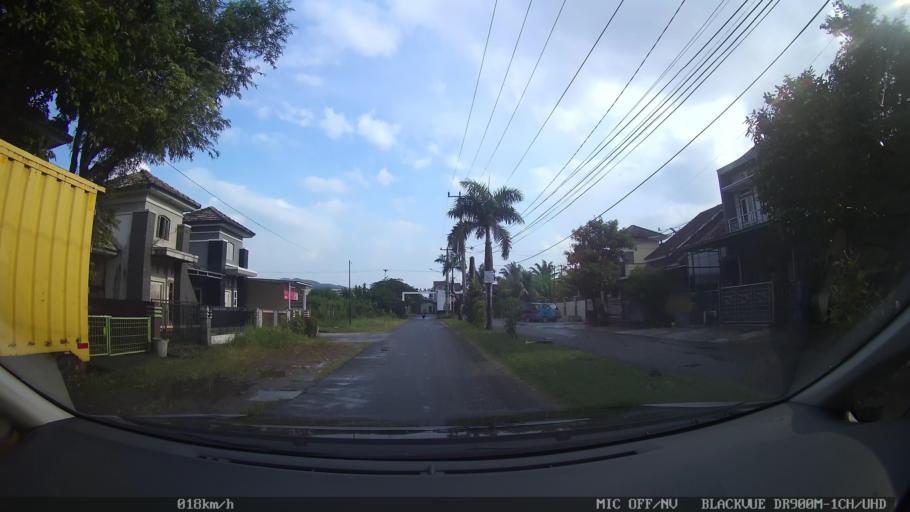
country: ID
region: Lampung
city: Kedaton
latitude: -5.3899
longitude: 105.3056
